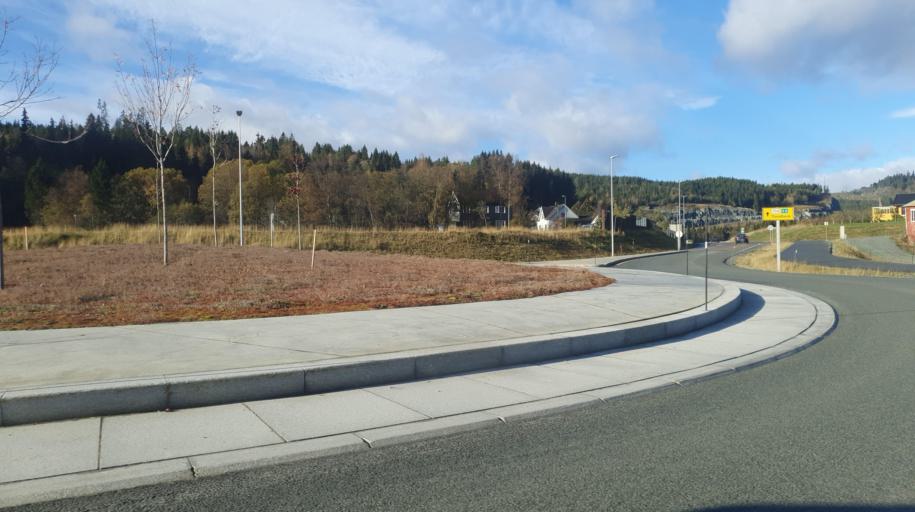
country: NO
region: Sor-Trondelag
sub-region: Klaebu
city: Klaebu
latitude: 63.3135
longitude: 10.4304
